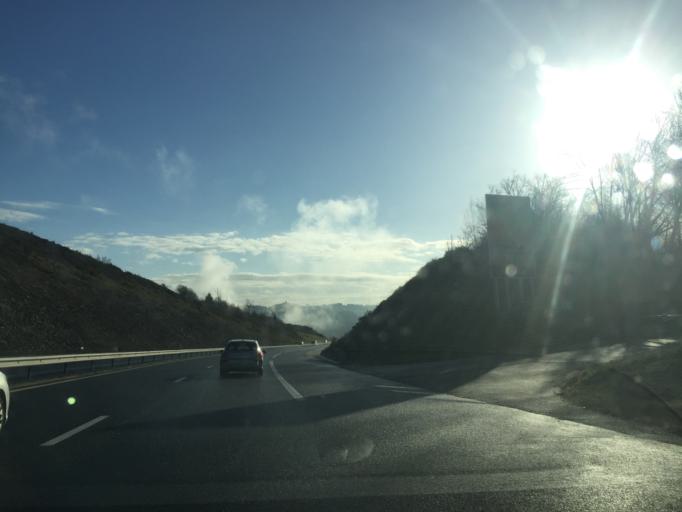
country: FR
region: Limousin
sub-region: Departement de la Correze
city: Naves
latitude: 45.3229
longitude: 1.7809
